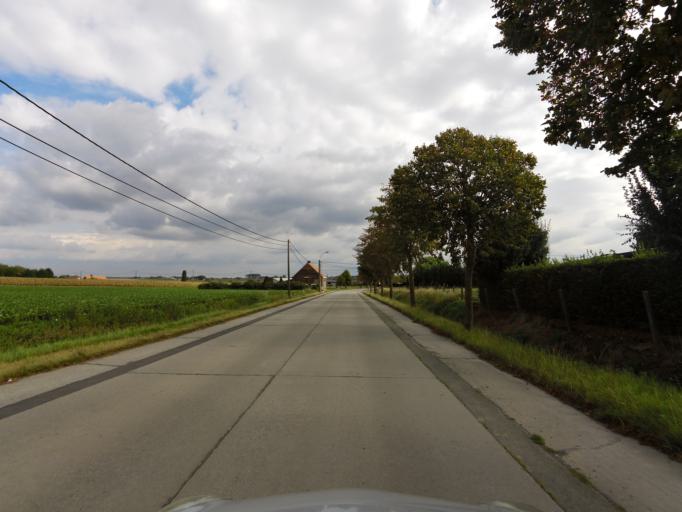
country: BE
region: Flanders
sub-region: Provincie West-Vlaanderen
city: Pittem
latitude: 51.0124
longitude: 3.2840
